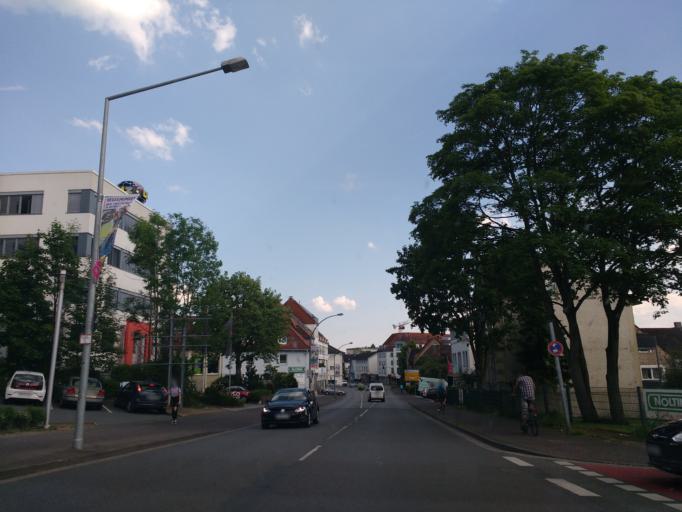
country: DE
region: North Rhine-Westphalia
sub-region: Regierungsbezirk Detmold
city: Detmold
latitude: 51.9440
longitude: 8.8757
